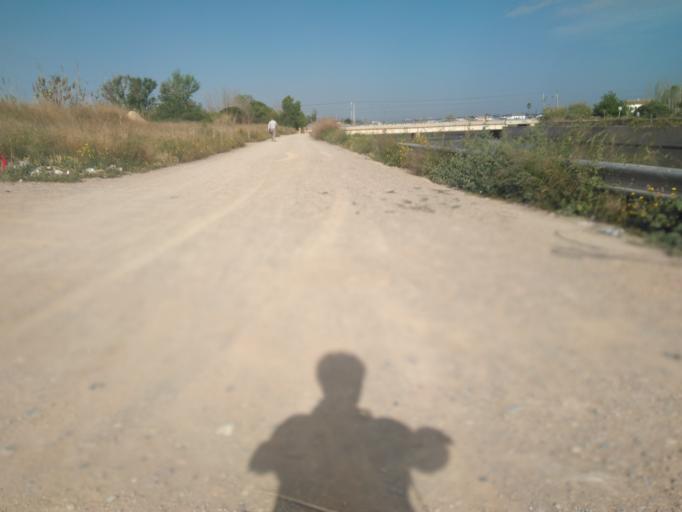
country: ES
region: Valencia
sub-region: Provincia de Valencia
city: Alboraya
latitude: 39.5017
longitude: -0.3264
